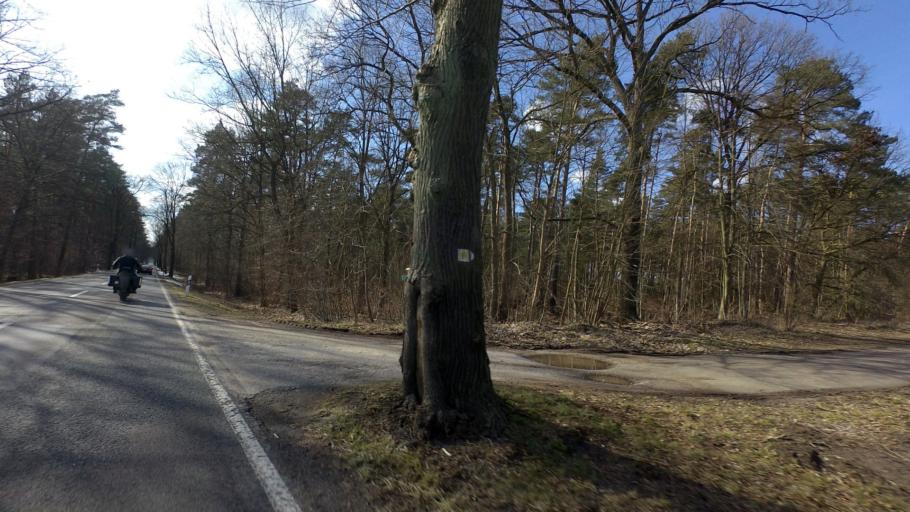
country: DE
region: Brandenburg
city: Biesenthal
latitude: 52.7643
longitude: 13.5924
